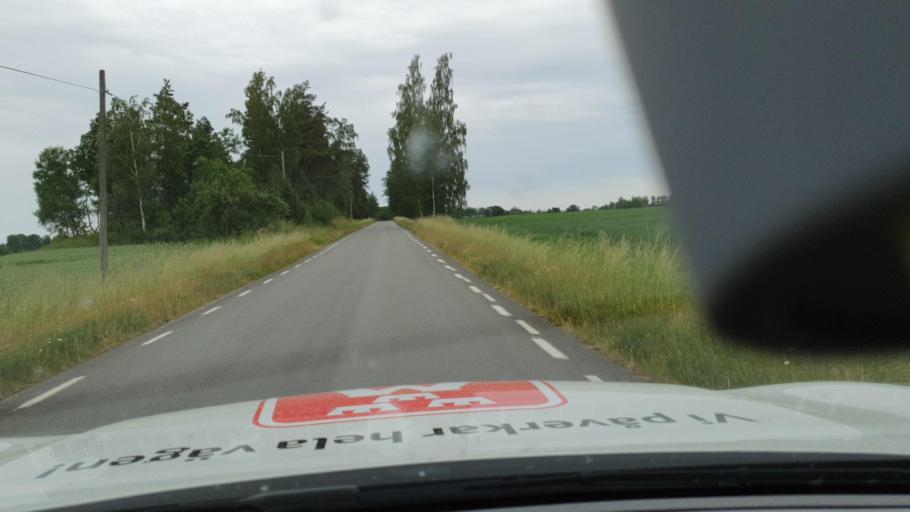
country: SE
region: Vaestra Goetaland
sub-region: Tidaholms Kommun
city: Olofstorp
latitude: 58.3163
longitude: 14.0964
